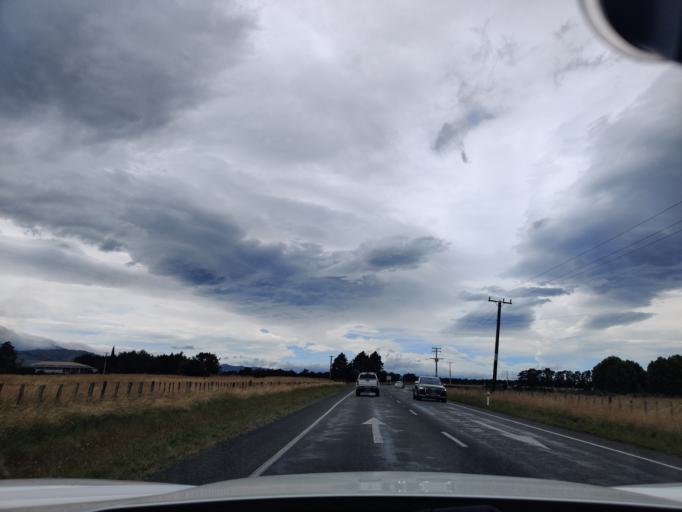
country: NZ
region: Wellington
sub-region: Masterton District
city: Masterton
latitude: -41.0012
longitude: 175.5568
